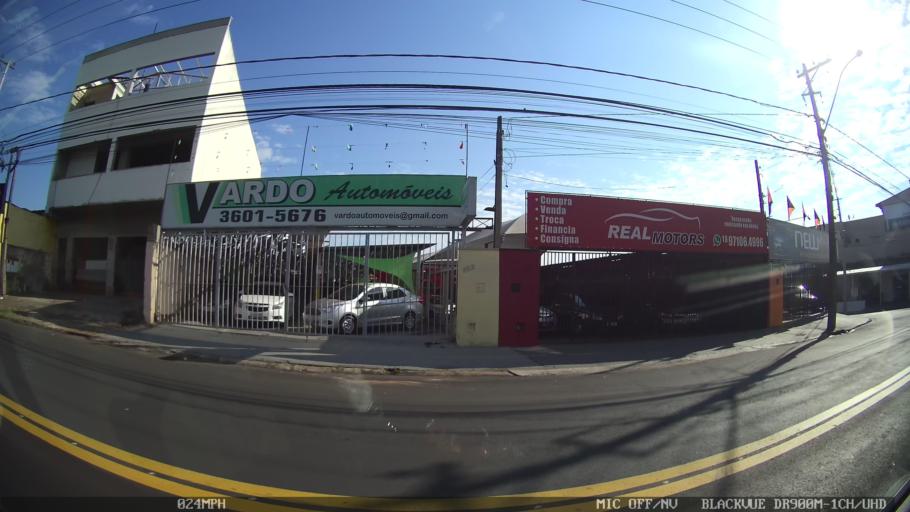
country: BR
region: Sao Paulo
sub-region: Americana
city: Americana
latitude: -22.7306
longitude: -47.3452
